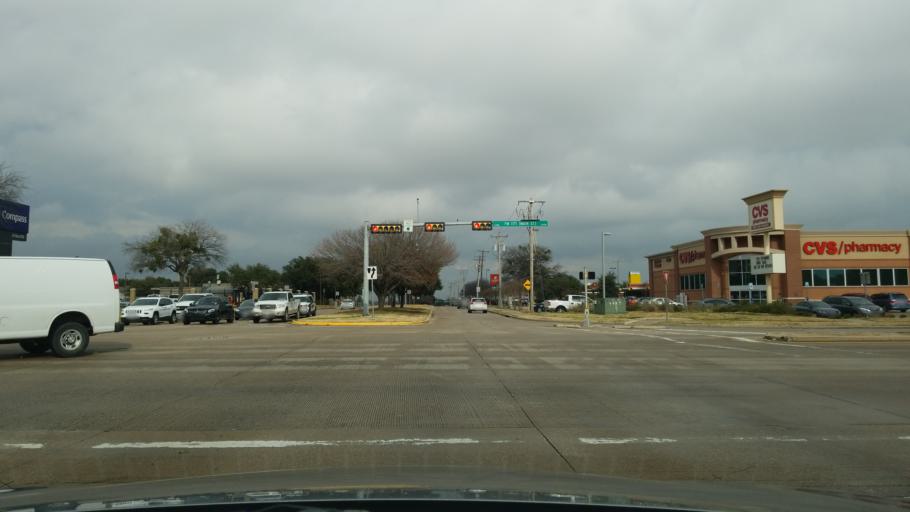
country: US
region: Texas
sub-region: Denton County
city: Lewisville
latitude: 33.0419
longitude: -97.0205
